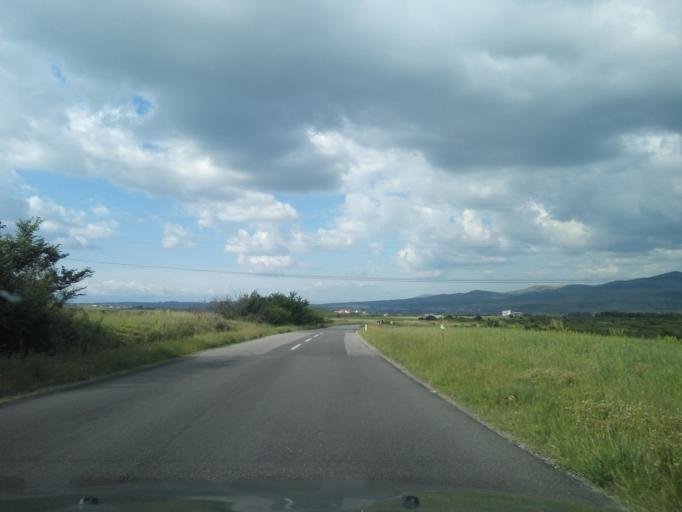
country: XK
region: Gjakova
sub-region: Komuna e Gjakoves
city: Gjakove
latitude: 42.4462
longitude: 20.4928
